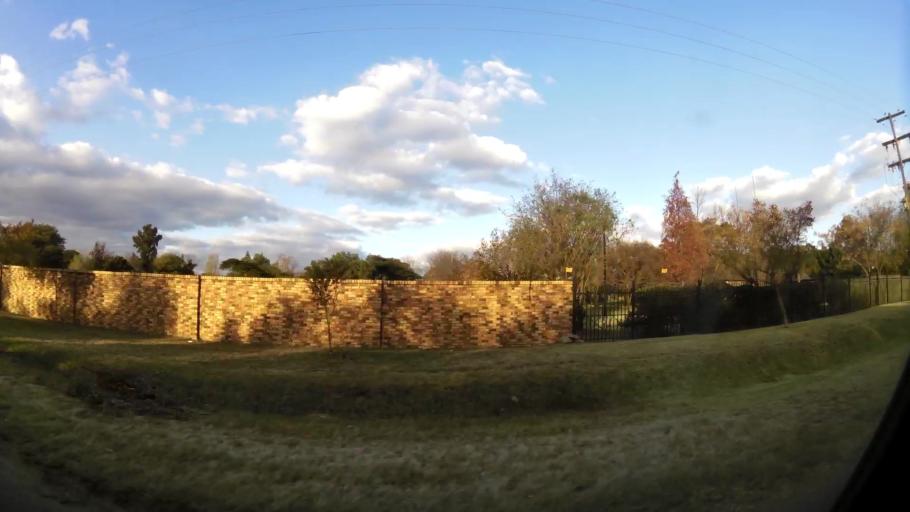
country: ZA
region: Gauteng
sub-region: City of Johannesburg Metropolitan Municipality
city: Midrand
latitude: -25.9738
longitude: 28.1533
